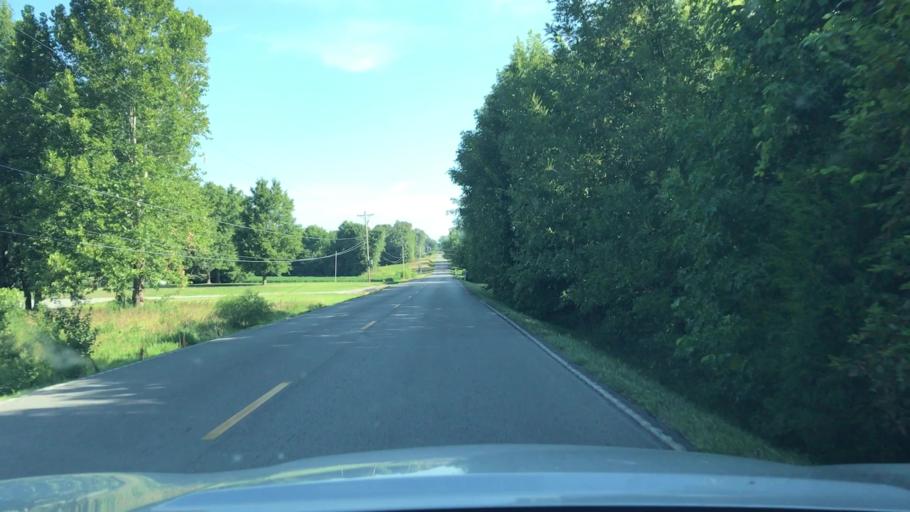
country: US
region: Kentucky
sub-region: Muhlenberg County
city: Greenville
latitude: 37.1506
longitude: -87.1415
